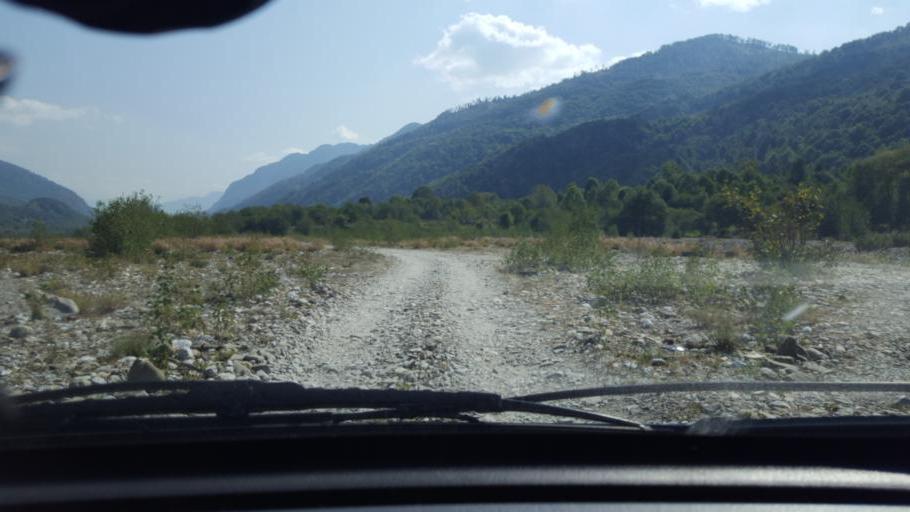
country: ME
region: Andrijevica
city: Andrijevica
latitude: 42.5945
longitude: 19.6764
